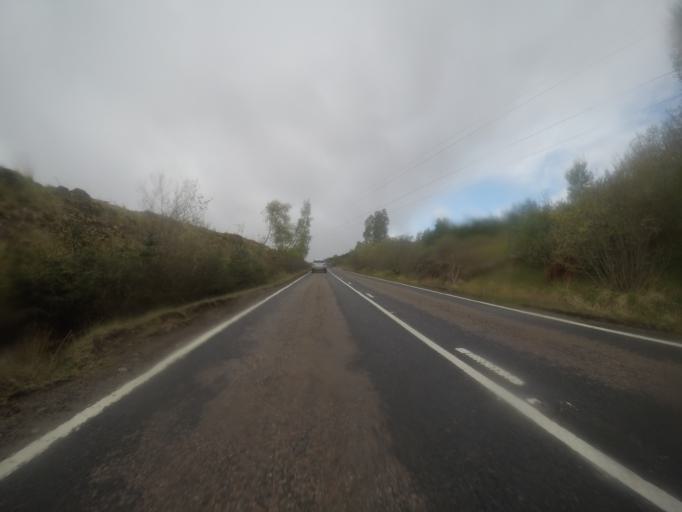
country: GB
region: Scotland
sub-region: Highland
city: Spean Bridge
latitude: 57.0833
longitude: -4.9057
